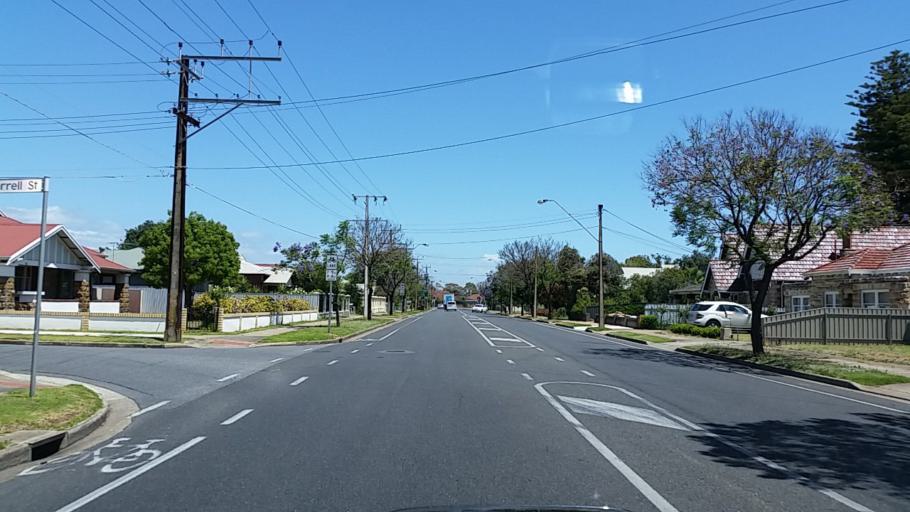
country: AU
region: South Australia
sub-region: Charles Sturt
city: Allenby Gardens
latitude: -34.9020
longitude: 138.5519
